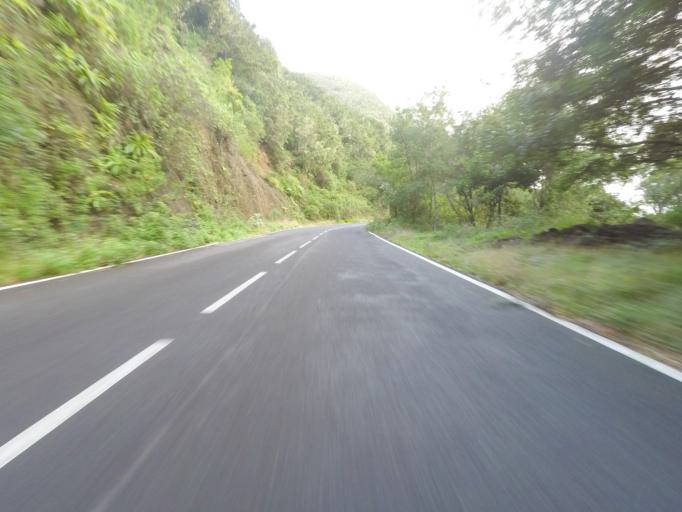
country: ES
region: Canary Islands
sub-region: Provincia de Santa Cruz de Tenerife
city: Hermigua
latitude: 28.1281
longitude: -17.2102
